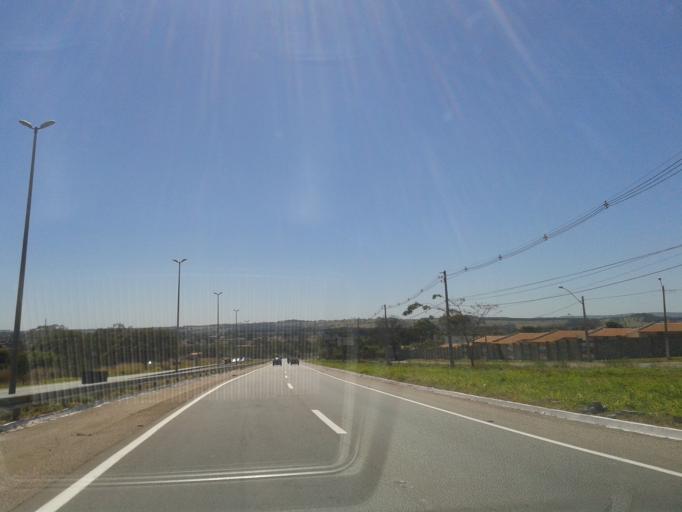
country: BR
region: Goias
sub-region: Goianira
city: Goianira
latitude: -16.6067
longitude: -49.3666
